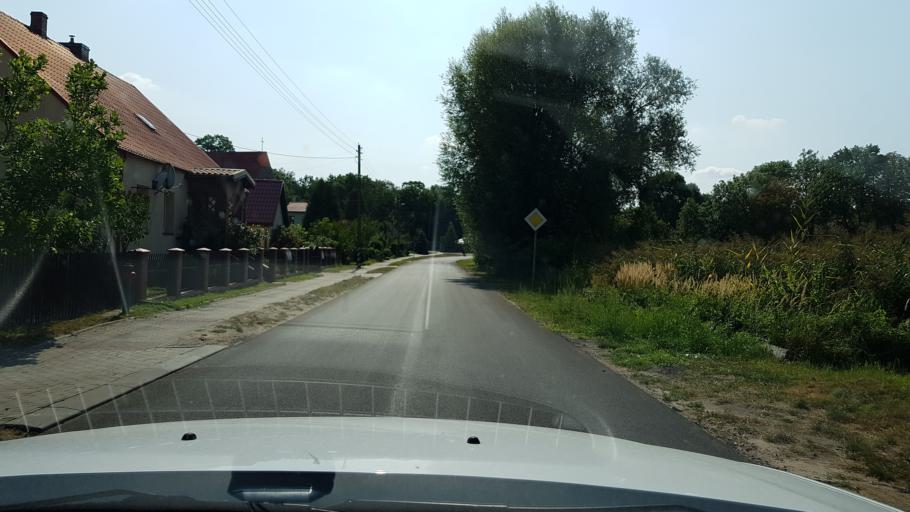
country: PL
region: West Pomeranian Voivodeship
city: Trzcinsko Zdroj
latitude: 52.9220
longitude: 14.5343
